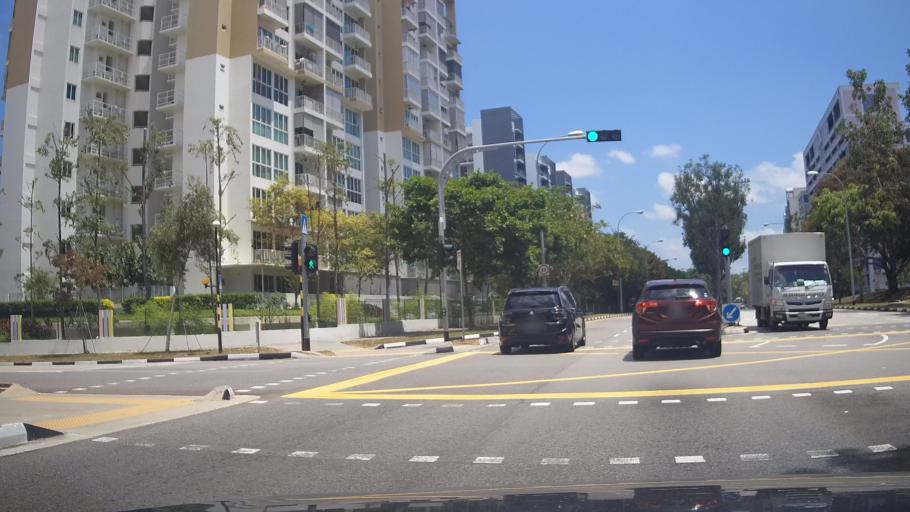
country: MY
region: Johor
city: Kampung Pasir Gudang Baru
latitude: 1.3756
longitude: 103.9589
